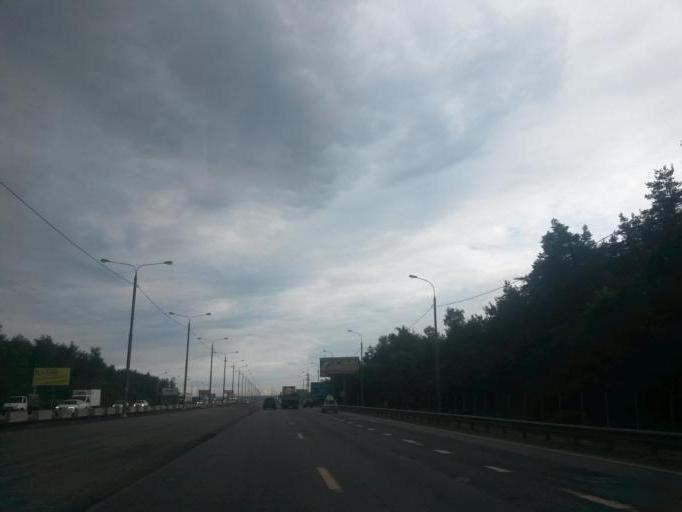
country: RU
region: Moskovskaya
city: Shcherbinka
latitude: 55.4906
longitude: 37.6117
